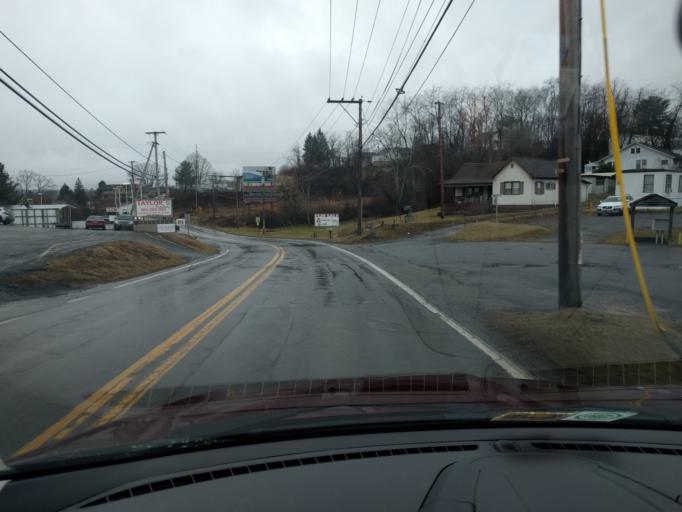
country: US
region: West Virginia
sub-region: Raleigh County
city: Beckley
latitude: 37.7934
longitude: -81.1767
